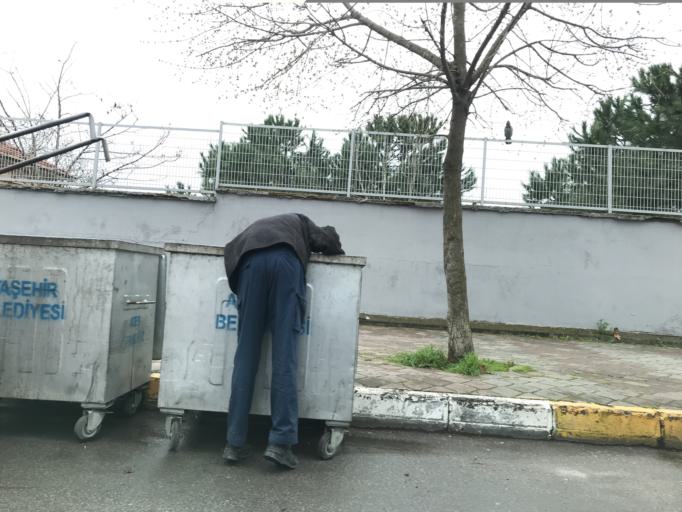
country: TR
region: Istanbul
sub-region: Atasehir
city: Atasehir
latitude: 40.9860
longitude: 29.0965
